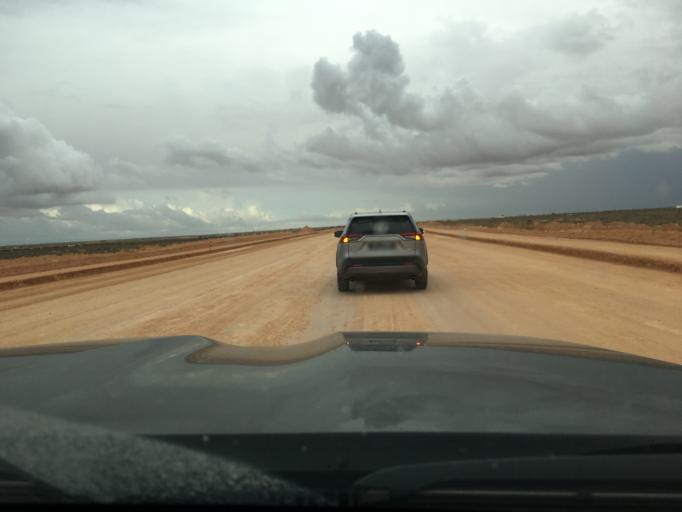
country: TN
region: Madanin
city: Medenine
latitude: 33.2795
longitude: 10.5939
